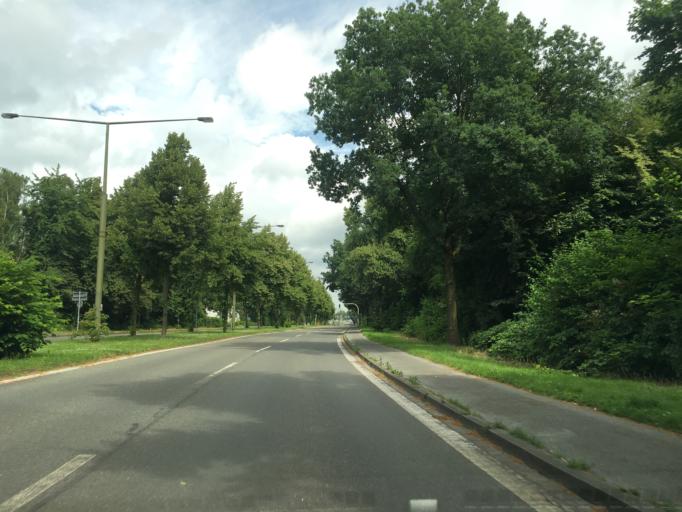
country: DE
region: North Rhine-Westphalia
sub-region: Regierungsbezirk Munster
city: Gelsenkirchen
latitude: 51.5402
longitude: 7.1089
